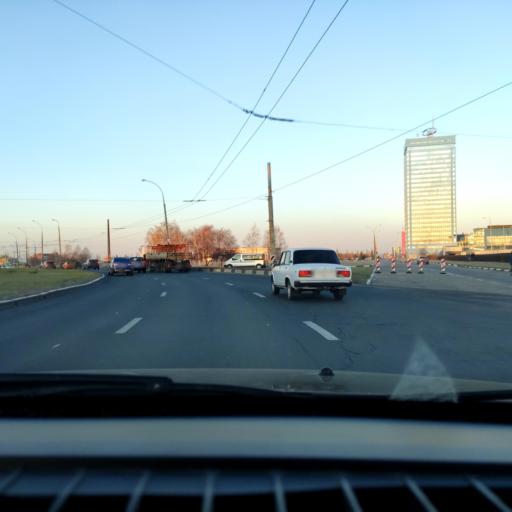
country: RU
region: Samara
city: Tol'yatti
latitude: 53.5550
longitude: 49.2715
